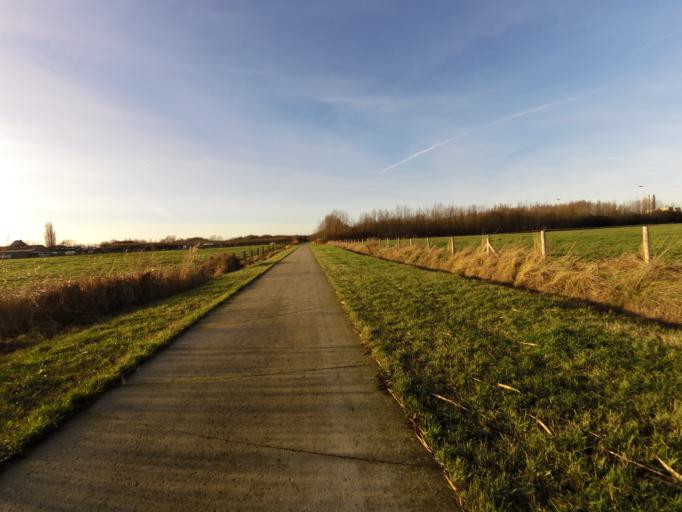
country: BE
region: Flanders
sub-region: Provincie West-Vlaanderen
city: Bredene
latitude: 51.2042
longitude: 2.9704
